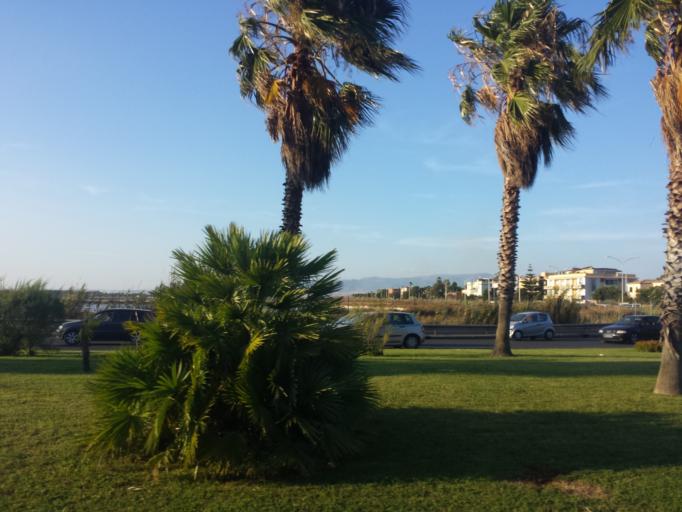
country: IT
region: Sardinia
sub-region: Provincia di Cagliari
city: Cagliari
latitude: 39.1942
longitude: 9.1563
